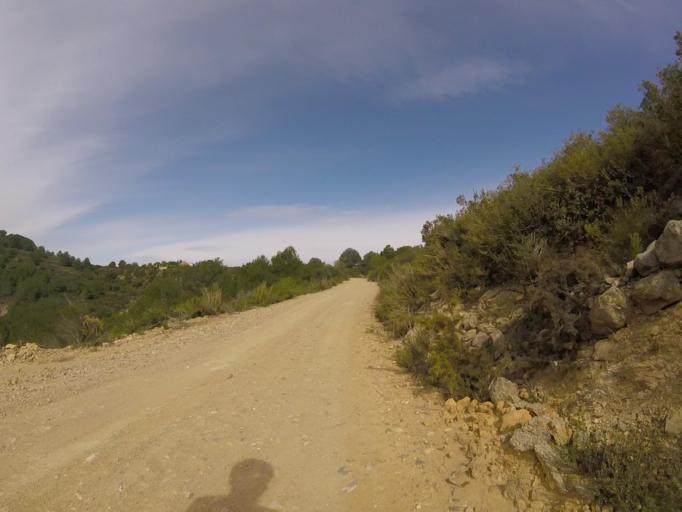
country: ES
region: Valencia
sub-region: Provincia de Castello
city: Torreblanca
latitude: 40.2049
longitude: 0.1495
